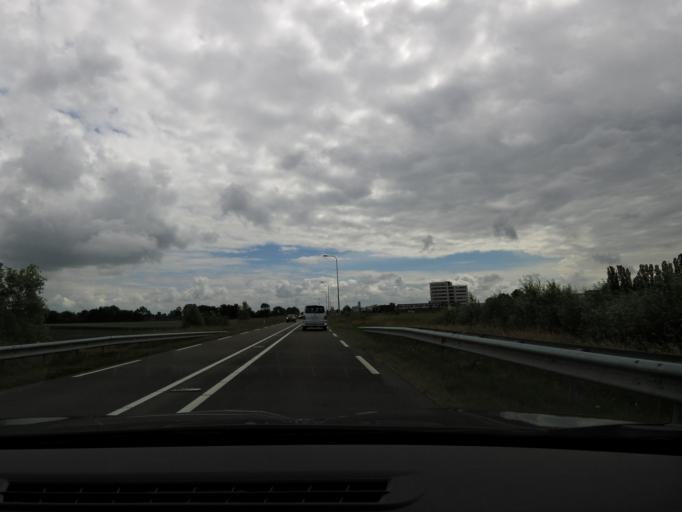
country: NL
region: Zeeland
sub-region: Gemeente Vlissingen
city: Vlissingen
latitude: 51.4719
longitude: 3.5666
